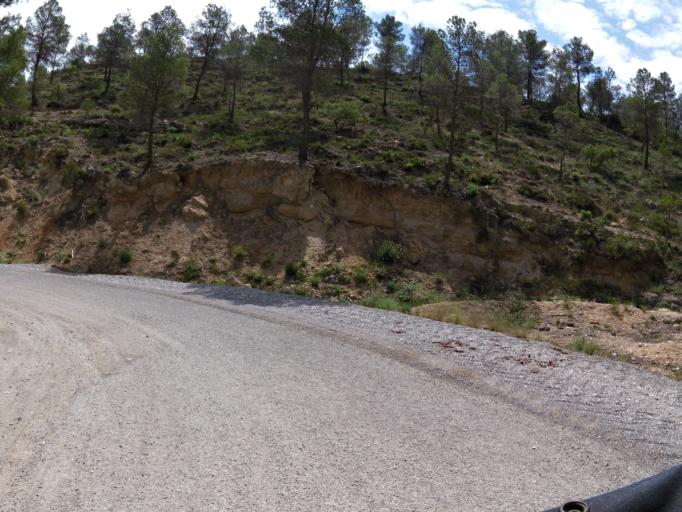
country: ES
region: Castille-La Mancha
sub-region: Provincia de Albacete
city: Casas Ibanez
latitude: 39.3670
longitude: -1.4599
